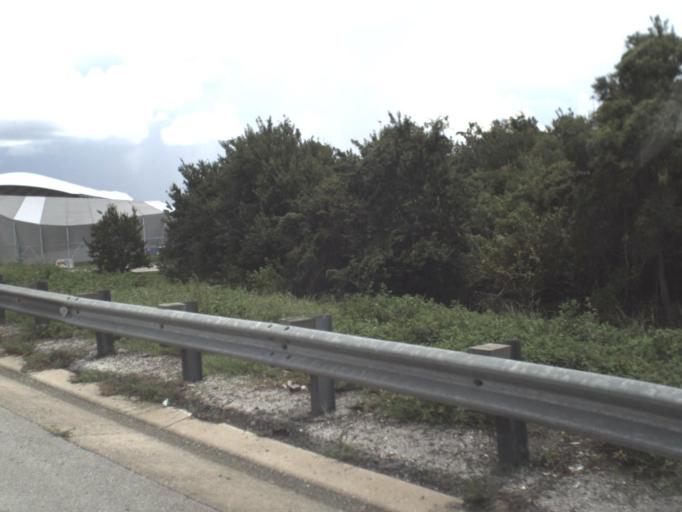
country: US
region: Florida
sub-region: Hillsborough County
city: East Lake-Orient Park
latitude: 27.9959
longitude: -82.3684
